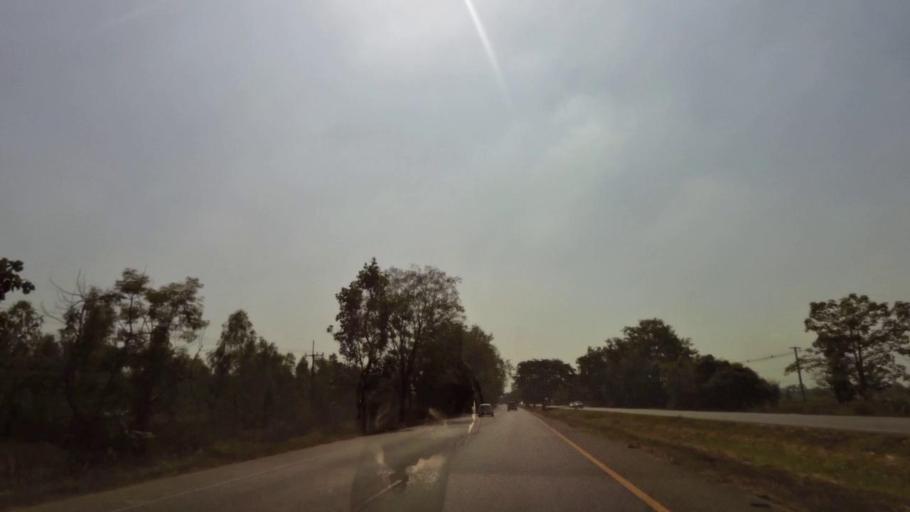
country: TH
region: Phichit
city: Wachira Barami
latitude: 16.3680
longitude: 100.1319
